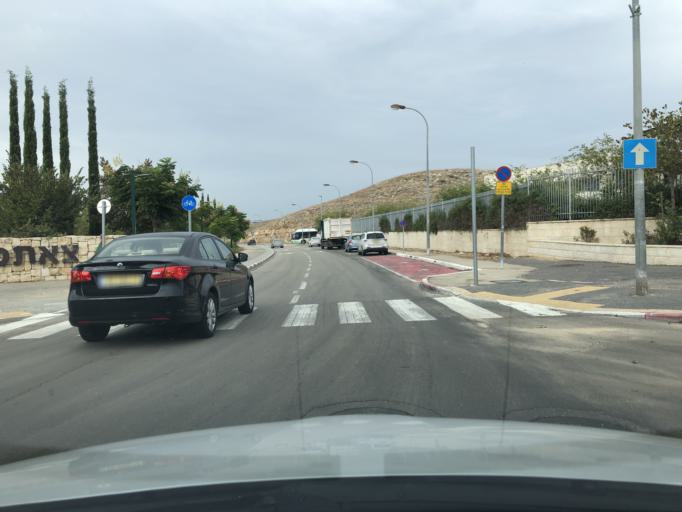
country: PS
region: West Bank
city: Al Midyah
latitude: 31.9179
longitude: 35.0029
